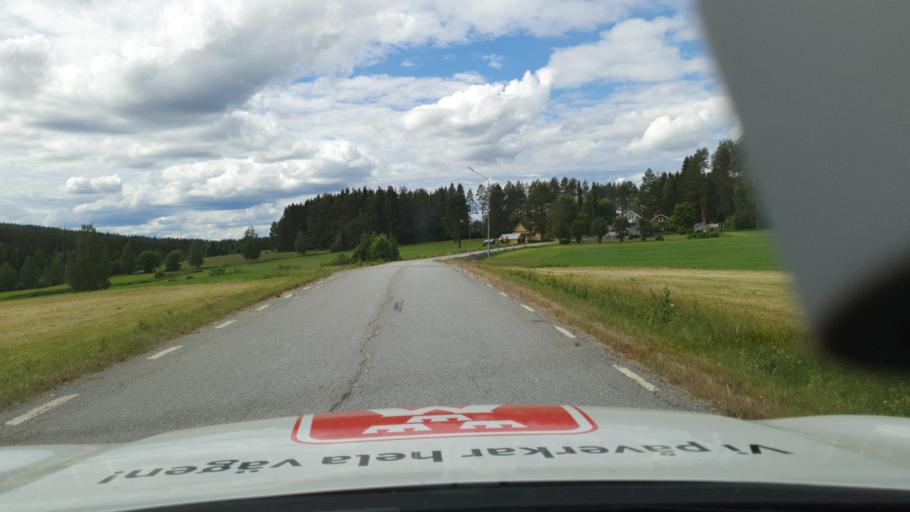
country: SE
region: Vaesterbotten
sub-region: Bjurholms Kommun
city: Bjurholm
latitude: 63.9165
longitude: 19.0730
